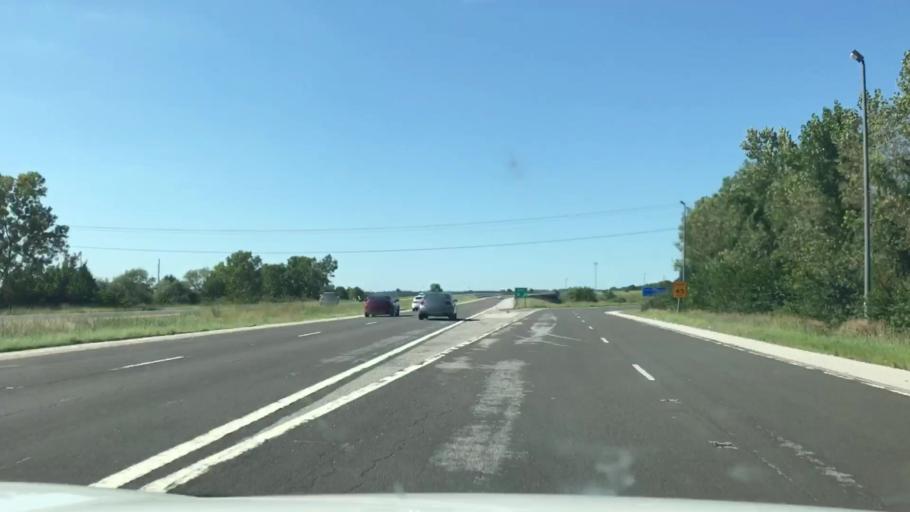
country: US
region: Illinois
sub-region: Madison County
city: South Roxana
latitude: 38.8467
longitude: -90.0486
